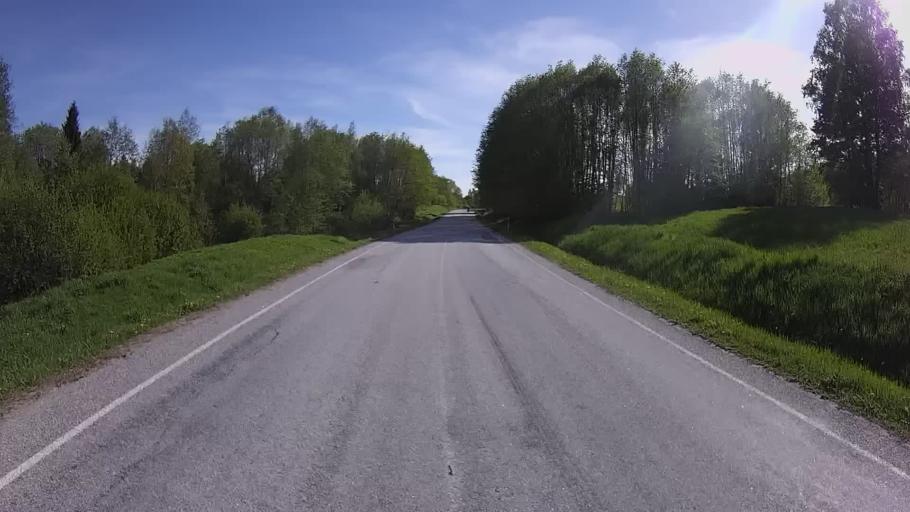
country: EE
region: Vorumaa
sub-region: Antsla vald
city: Vana-Antsla
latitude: 58.0280
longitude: 26.5101
